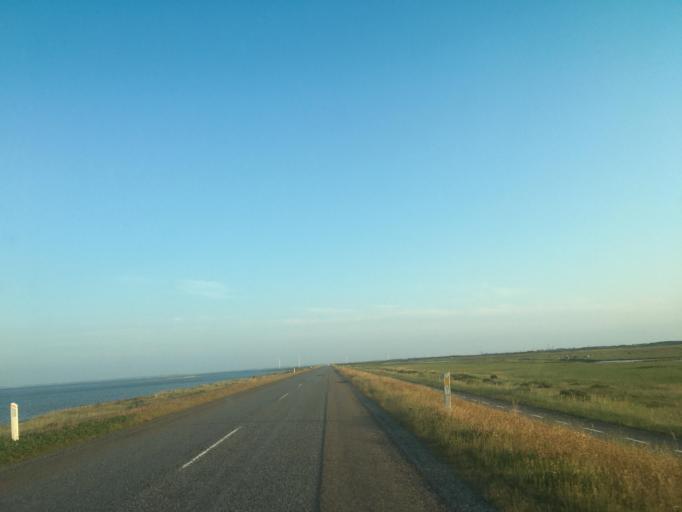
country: DK
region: Central Jutland
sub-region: Lemvig Kommune
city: Thyboron
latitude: 56.7364
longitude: 8.2501
